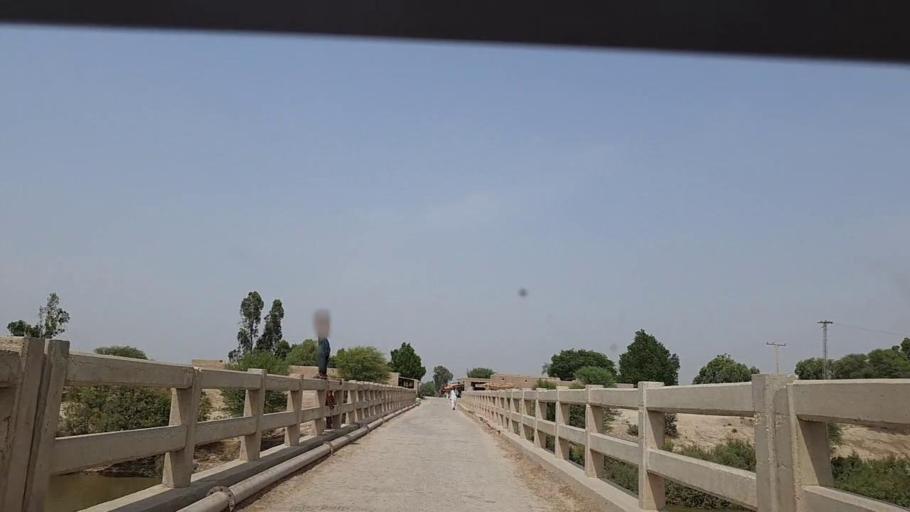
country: PK
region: Sindh
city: Khairpur Nathan Shah
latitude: 27.0755
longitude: 67.6516
